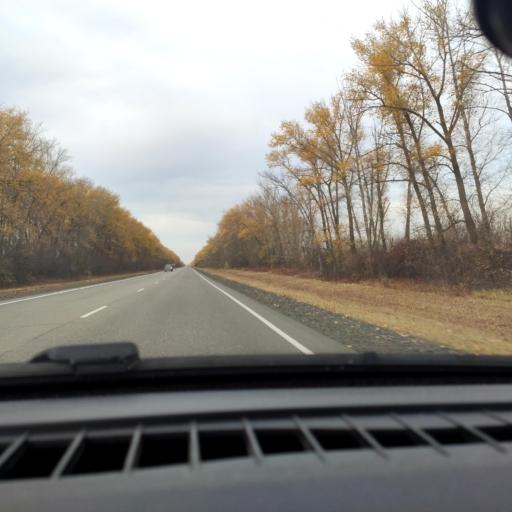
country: RU
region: Voronezj
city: Ostrogozhsk
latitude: 50.9814
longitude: 38.9948
